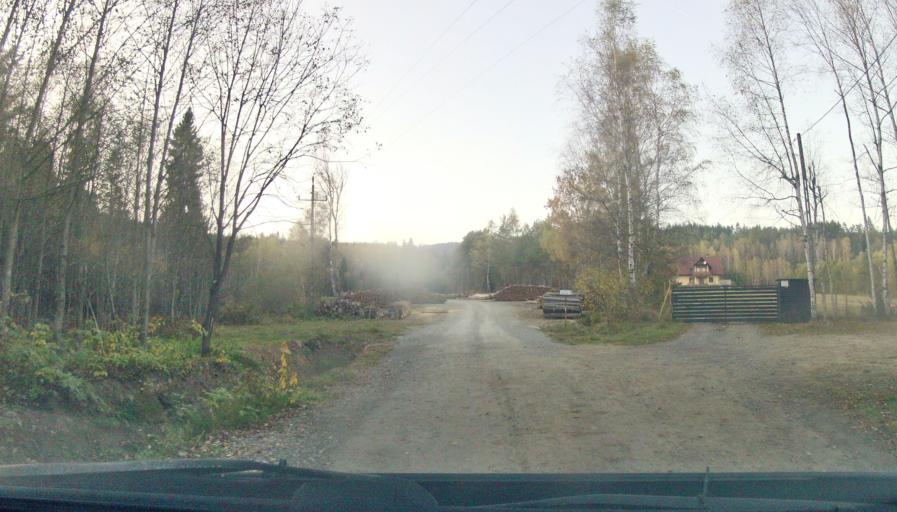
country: PL
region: Silesian Voivodeship
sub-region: Powiat zywiecki
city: Slemien
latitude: 49.7404
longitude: 19.4143
